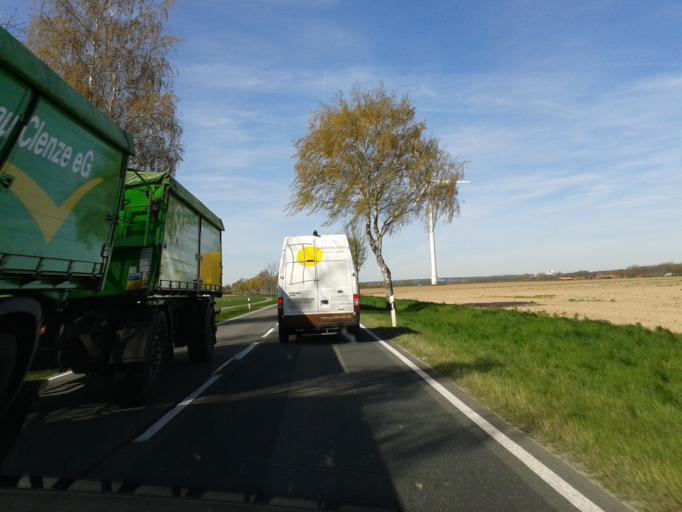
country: DE
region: Lower Saxony
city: Ratzlingen
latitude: 52.9579
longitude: 10.6443
